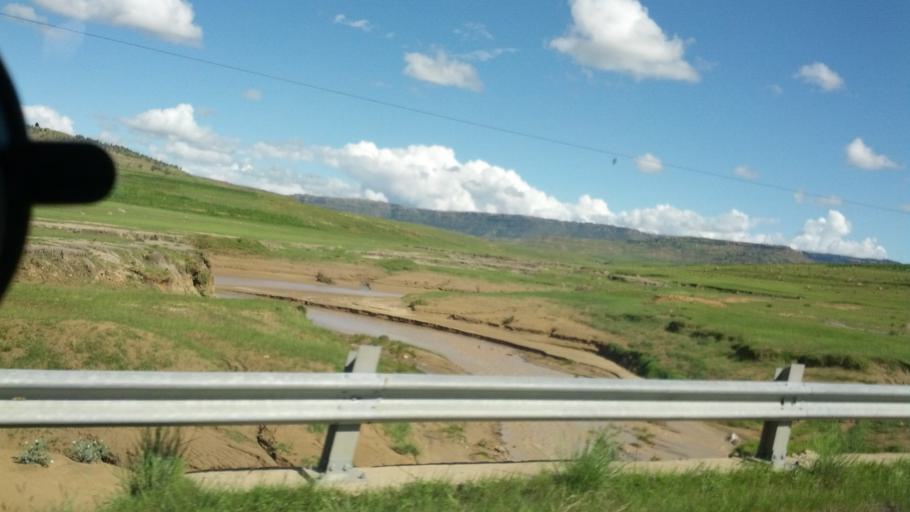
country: LS
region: Maseru
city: Maseru
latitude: -29.5506
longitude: 27.4978
